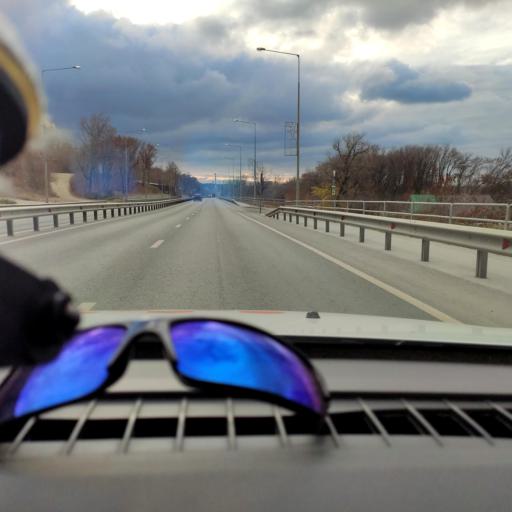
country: RU
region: Samara
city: Volzhskiy
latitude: 53.3964
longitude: 50.1520
